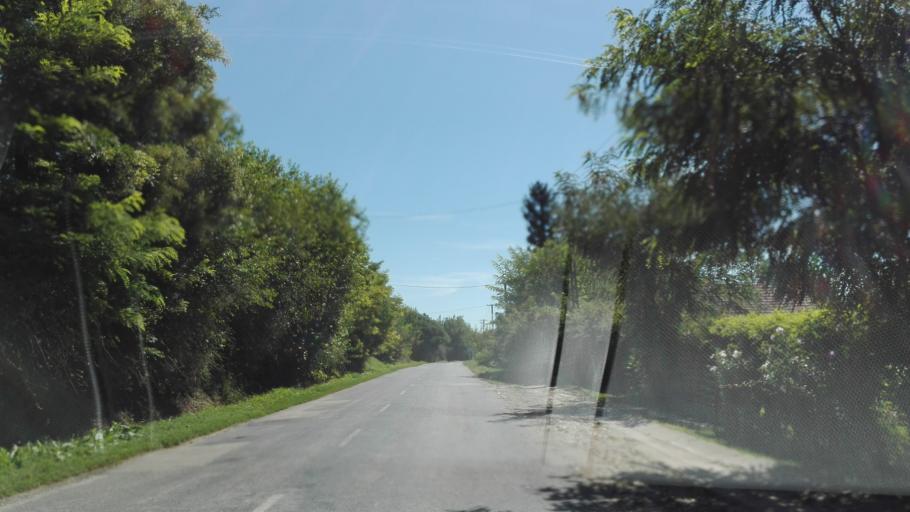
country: HU
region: Tolna
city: Ozora
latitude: 46.7497
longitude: 18.4471
